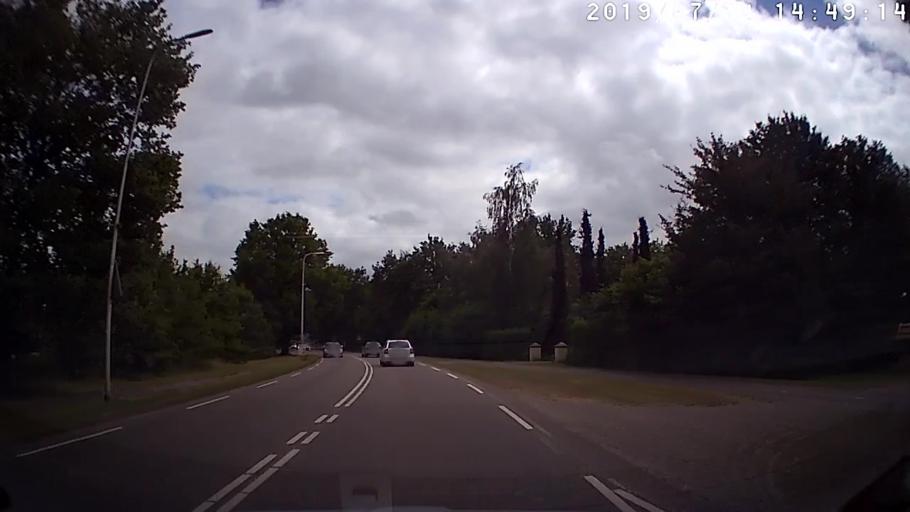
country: NL
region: Overijssel
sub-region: Gemeente Raalte
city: Heino
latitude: 52.4460
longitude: 6.2285
